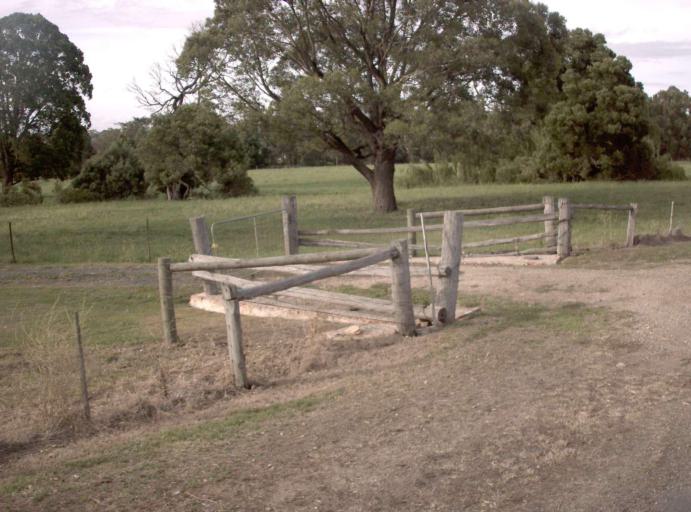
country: AU
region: Victoria
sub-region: Wellington
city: Heyfield
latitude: -37.9877
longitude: 146.7777
